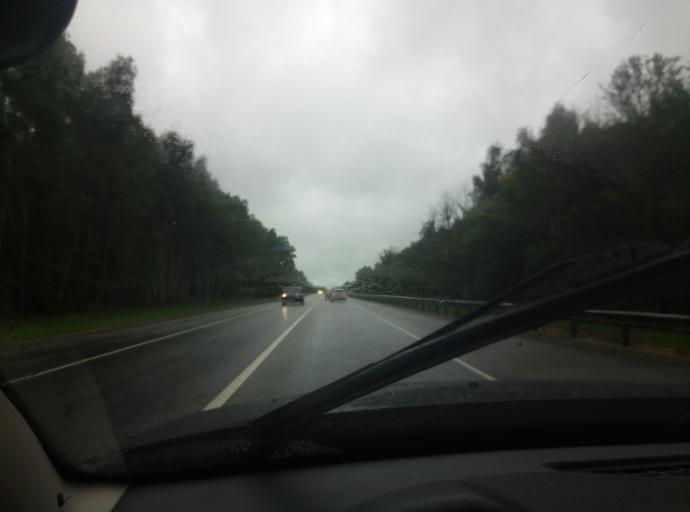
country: RU
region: Tula
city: Leninskiy
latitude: 54.3744
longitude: 37.5212
